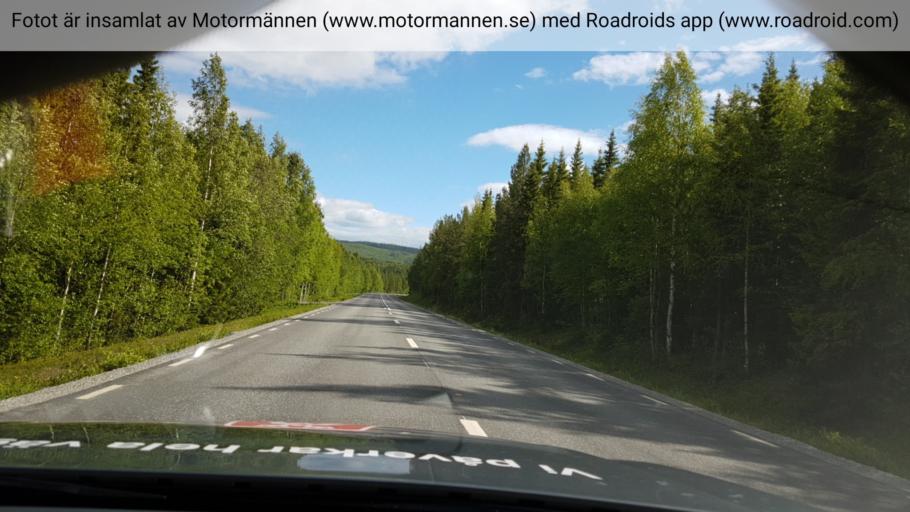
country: SE
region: Jaemtland
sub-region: Stroemsunds Kommun
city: Stroemsund
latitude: 64.1512
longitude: 15.6800
